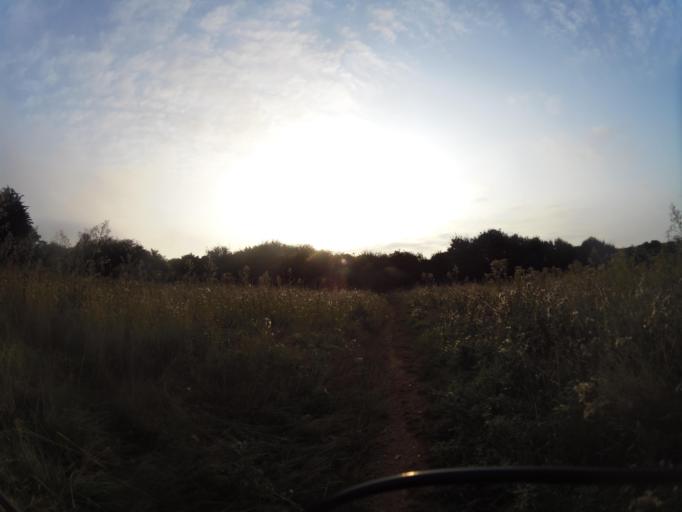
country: GB
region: England
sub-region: Suffolk
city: Bramford
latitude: 52.0362
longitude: 1.1045
